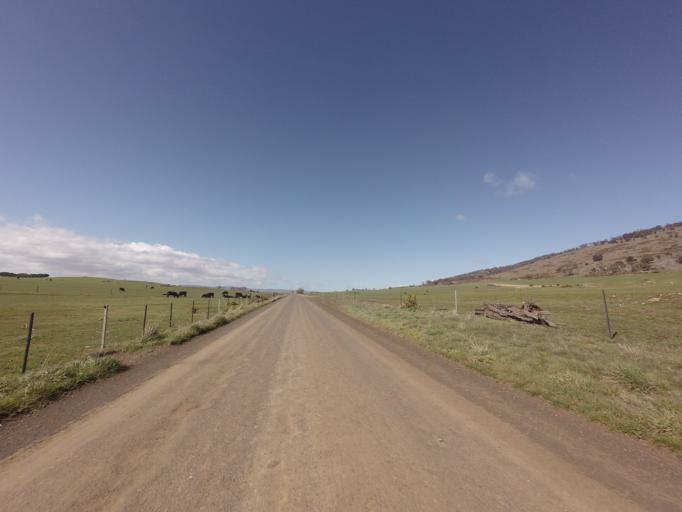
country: AU
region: Tasmania
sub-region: Northern Midlands
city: Evandale
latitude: -41.9191
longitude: 147.3948
